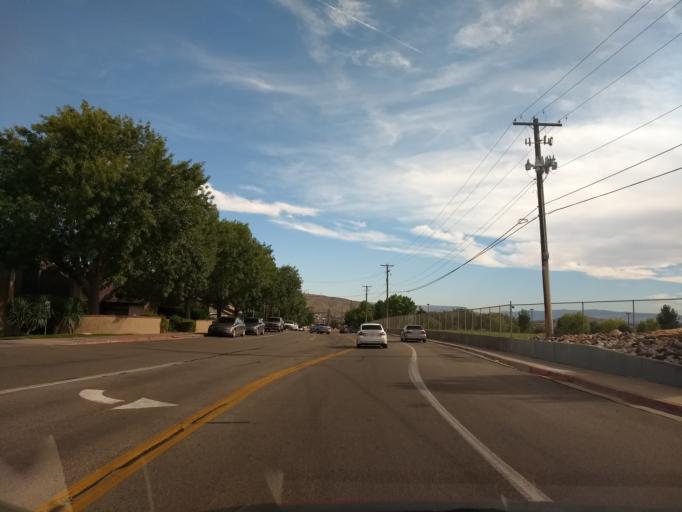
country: US
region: Utah
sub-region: Washington County
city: Saint George
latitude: 37.0961
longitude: -113.5749
